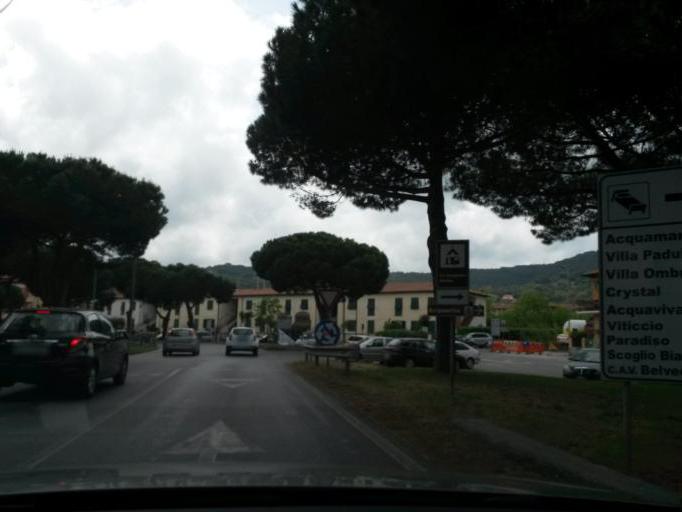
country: IT
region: Tuscany
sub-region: Provincia di Livorno
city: Portoferraio
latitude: 42.8103
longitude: 10.3094
